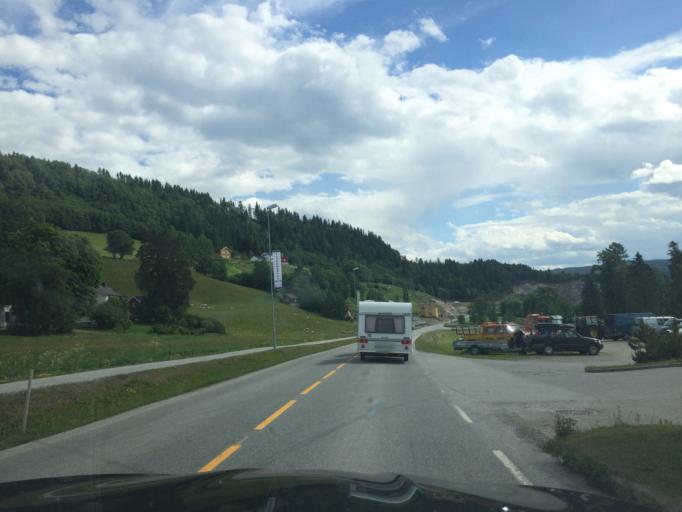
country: NO
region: Sor-Trondelag
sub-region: Selbu
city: Mebonden
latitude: 63.2182
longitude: 11.0428
